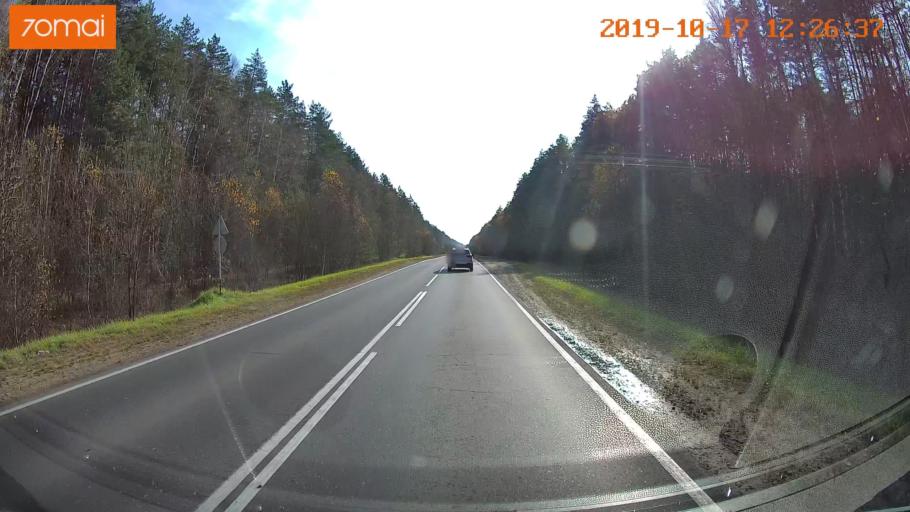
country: RU
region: Rjazan
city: Syntul
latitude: 55.0169
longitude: 41.2573
